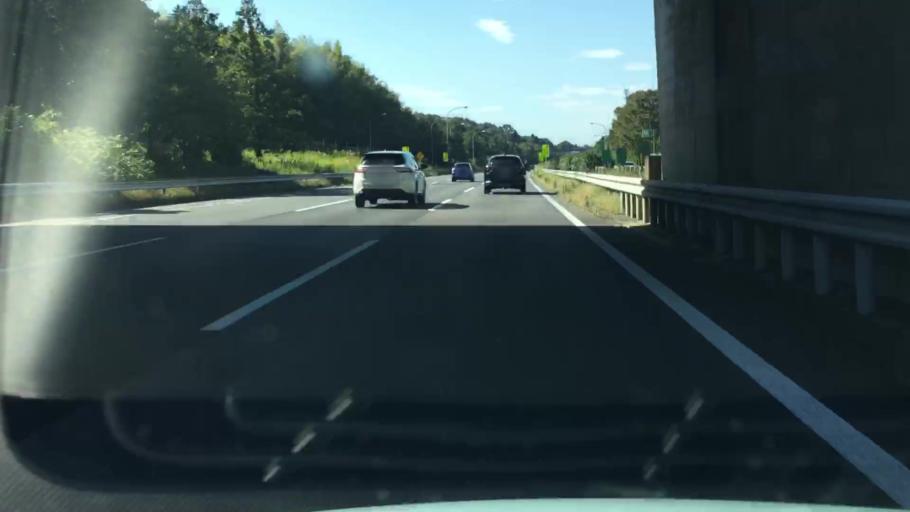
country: JP
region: Ibaraki
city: Ishioka
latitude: 36.1737
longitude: 140.2448
